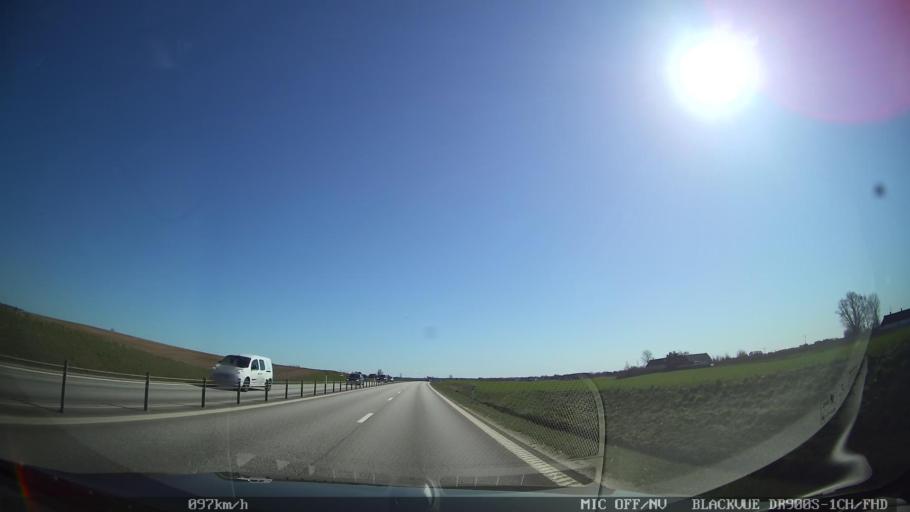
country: SE
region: Skane
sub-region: Skurups Kommun
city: Skurup
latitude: 55.4923
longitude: 13.5304
